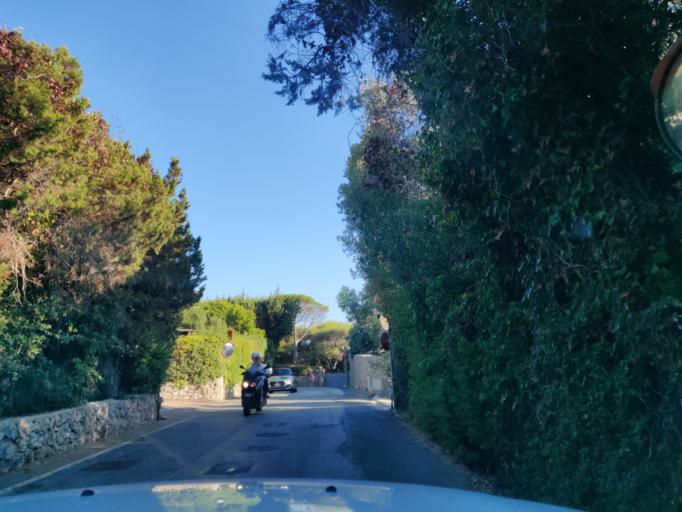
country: IT
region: Tuscany
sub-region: Provincia di Grosseto
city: Orbetello Scalo
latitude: 42.4097
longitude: 11.2809
